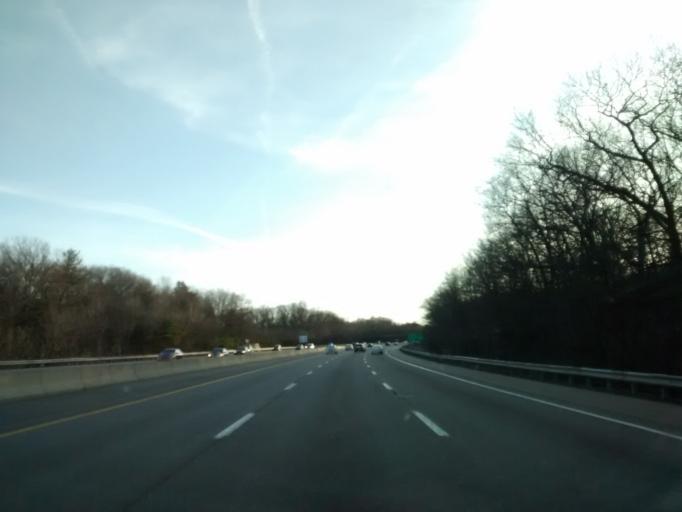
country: US
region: Massachusetts
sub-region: Worcester County
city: Cordaville
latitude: 42.2877
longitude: -71.4927
